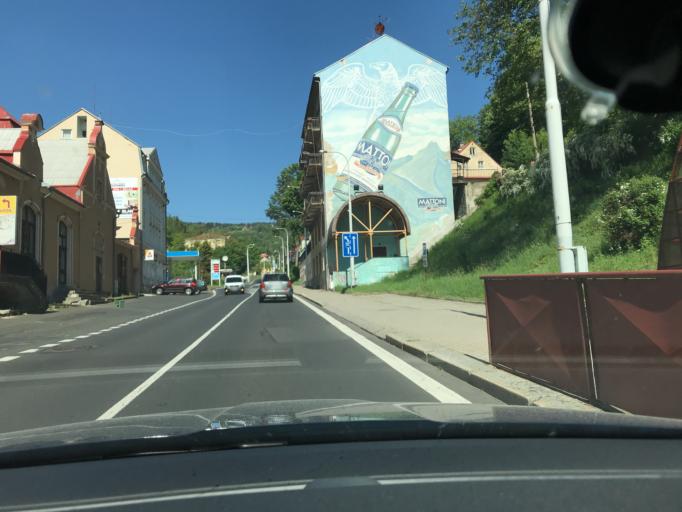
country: CZ
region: Karlovarsky
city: Jachymov
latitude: 50.3625
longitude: 12.9289
